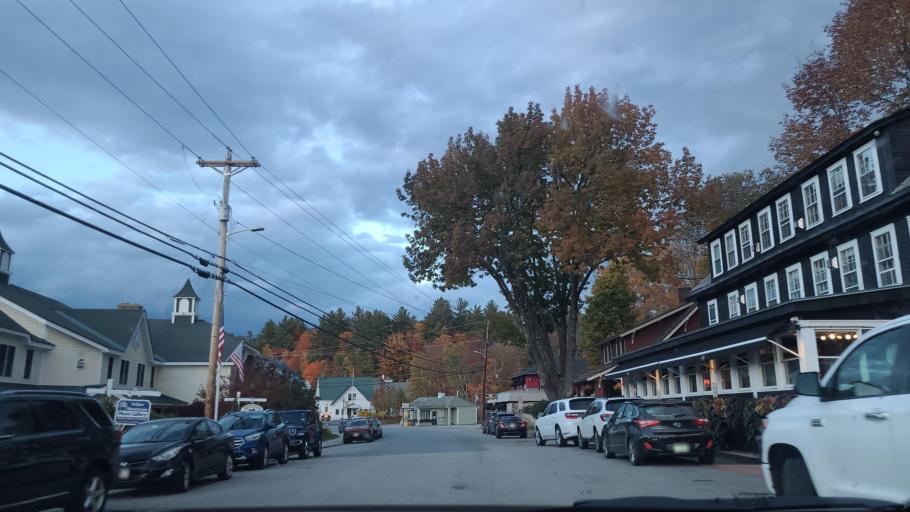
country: US
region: New Hampshire
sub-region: Carroll County
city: North Conway
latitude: 44.1449
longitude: -71.1806
